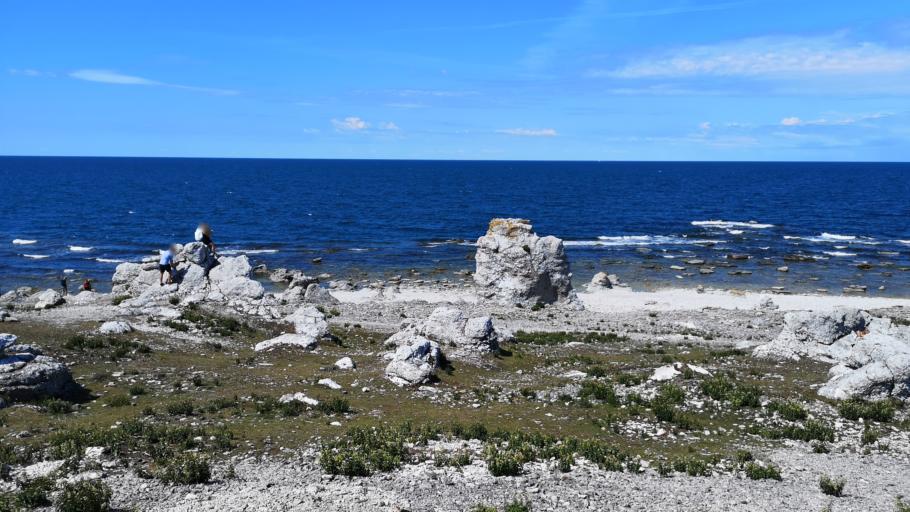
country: SE
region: Gotland
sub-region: Gotland
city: Slite
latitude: 57.9980
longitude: 19.1826
